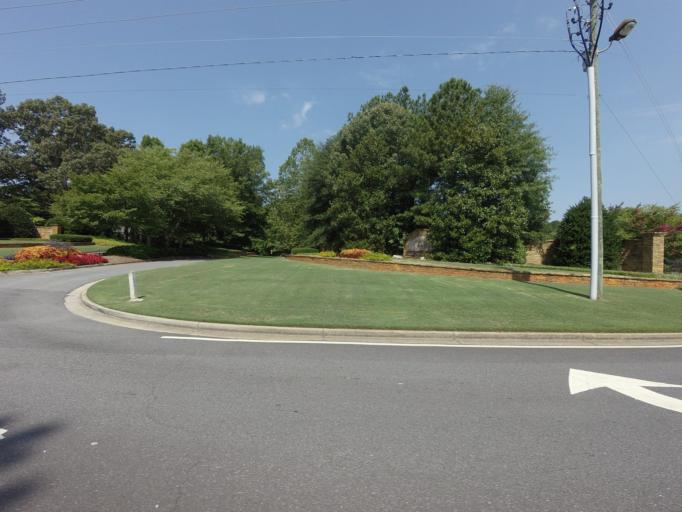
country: US
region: Georgia
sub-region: Fulton County
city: Alpharetta
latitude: 34.0145
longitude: -84.2810
